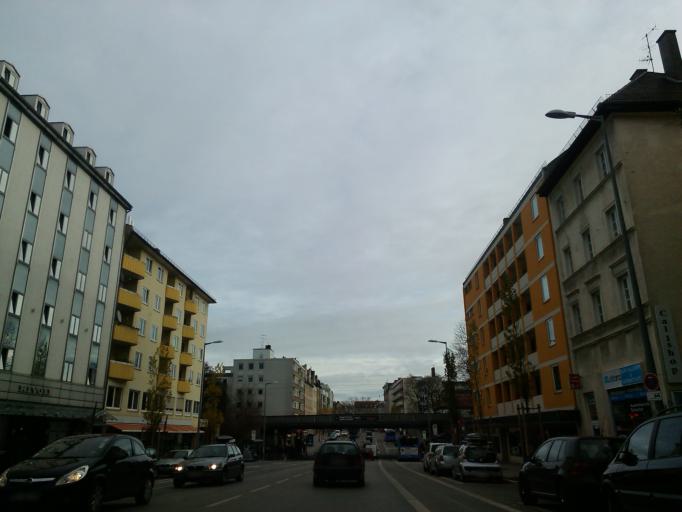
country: DE
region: Bavaria
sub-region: Upper Bavaria
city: Munich
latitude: 48.1169
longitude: 11.5348
